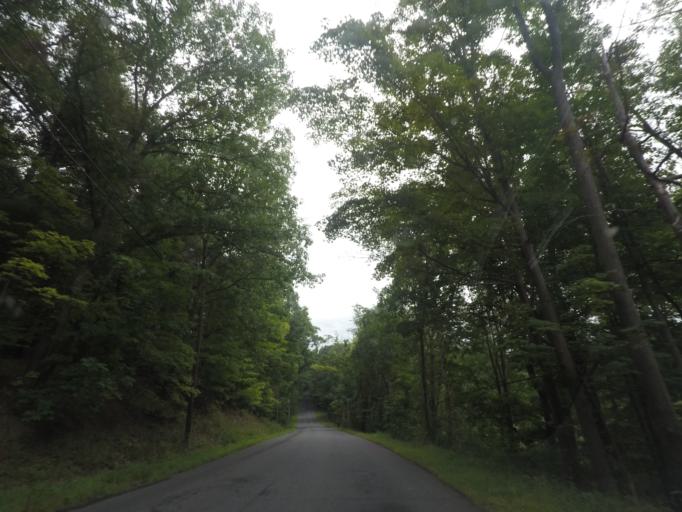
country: US
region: New York
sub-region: Rensselaer County
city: Nassau
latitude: 42.5045
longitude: -73.6072
